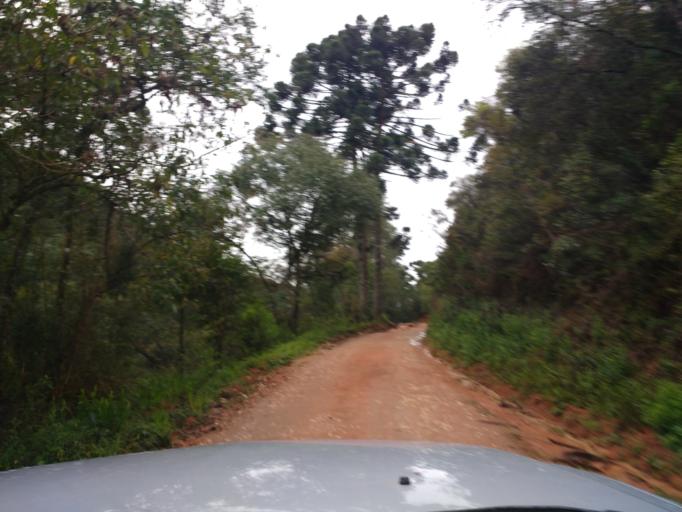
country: BR
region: Minas Gerais
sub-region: Cambui
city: Cambui
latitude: -22.7485
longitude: -45.9247
